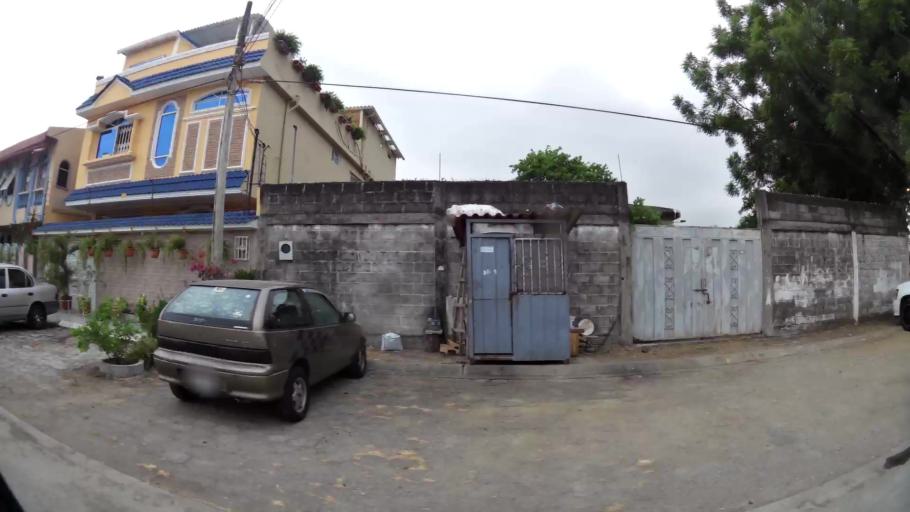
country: EC
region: Guayas
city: Eloy Alfaro
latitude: -2.1424
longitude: -79.9064
